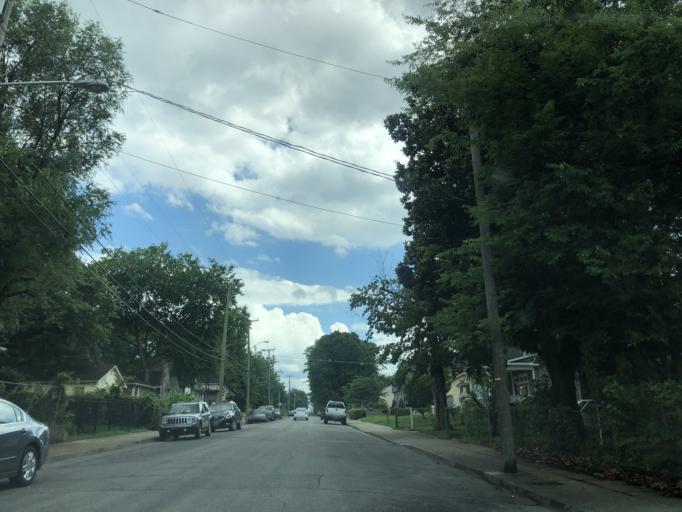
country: US
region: Tennessee
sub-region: Davidson County
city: Nashville
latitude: 36.1842
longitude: -86.7713
